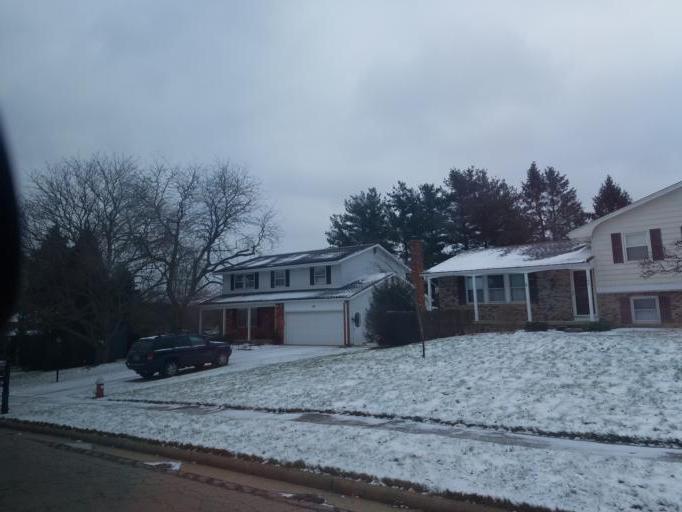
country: US
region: Ohio
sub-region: Richland County
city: Lexington
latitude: 40.6842
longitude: -82.6026
